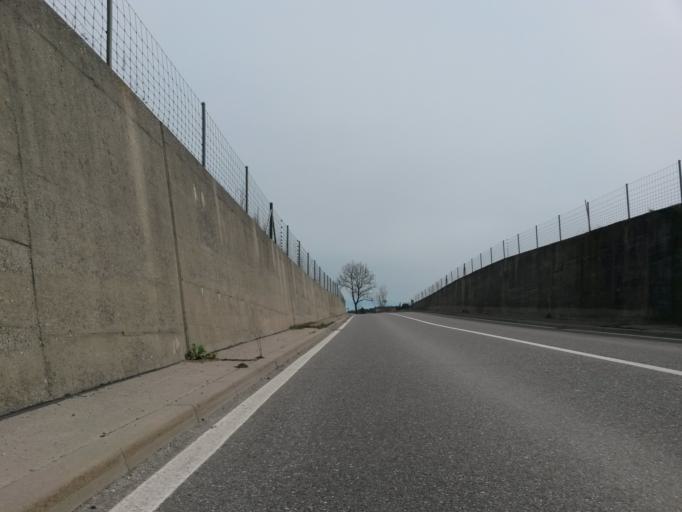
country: CH
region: Bern
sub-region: Biel/Bienne District
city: Lengnau
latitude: 47.1445
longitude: 7.3897
